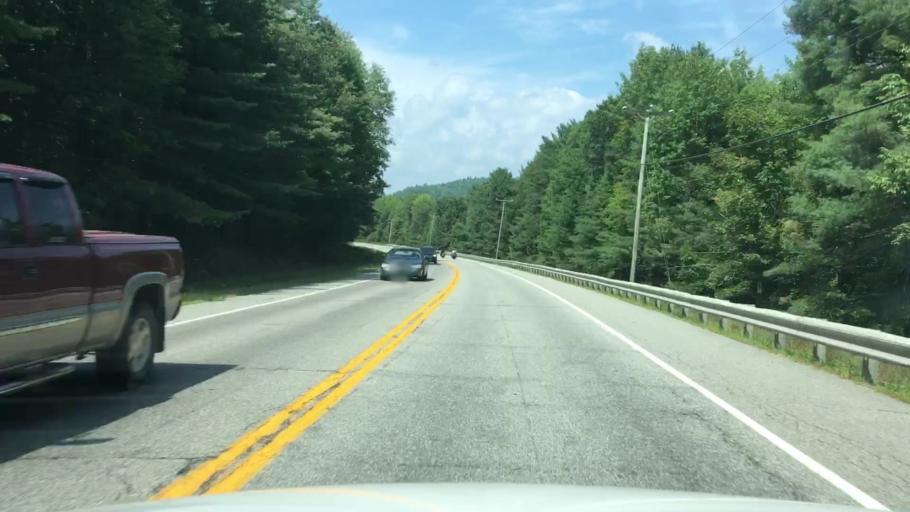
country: US
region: Maine
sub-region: Oxford County
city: Peru
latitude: 44.5089
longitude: -70.4070
